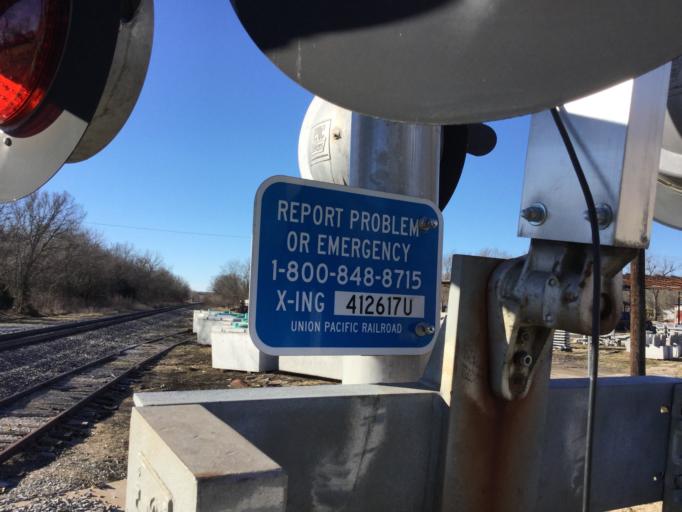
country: US
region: Kansas
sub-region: Miami County
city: Osawatomie
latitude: 38.3284
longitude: -94.9885
